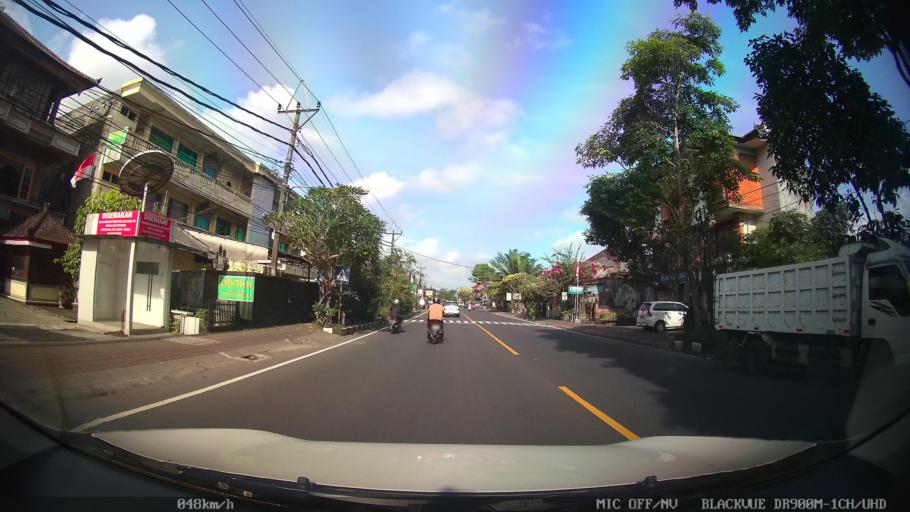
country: ID
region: Bali
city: Banjar Jumbayah
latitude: -8.5625
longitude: 115.1641
